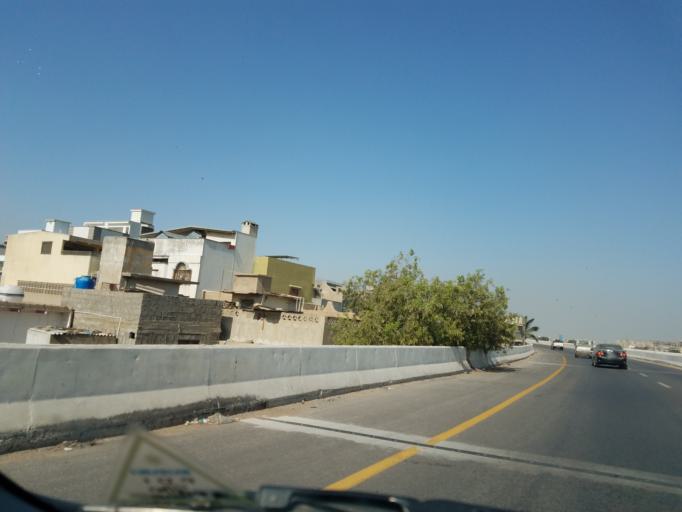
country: PK
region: Sindh
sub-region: Karachi District
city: Karachi
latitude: 24.8806
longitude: 67.0165
